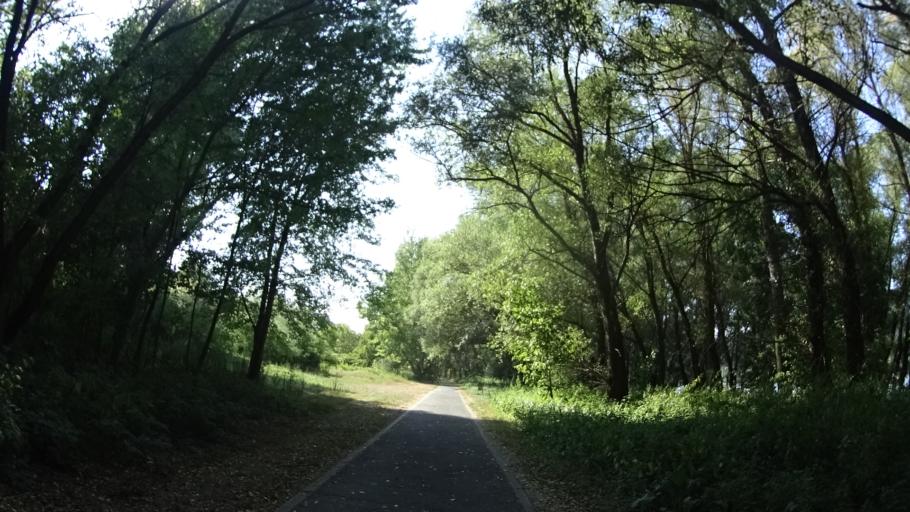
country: HU
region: Komarom-Esztergom
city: Esztergom
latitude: 47.8159
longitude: 18.7904
